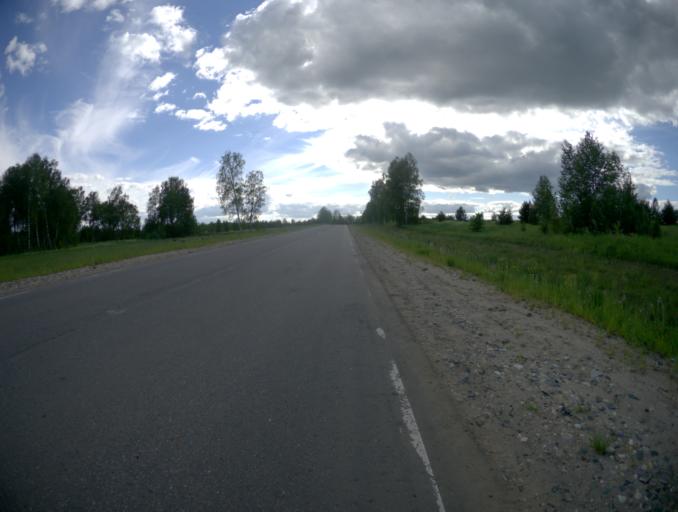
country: RU
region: Ivanovo
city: Novyye Gorki
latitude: 56.8024
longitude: 41.1382
